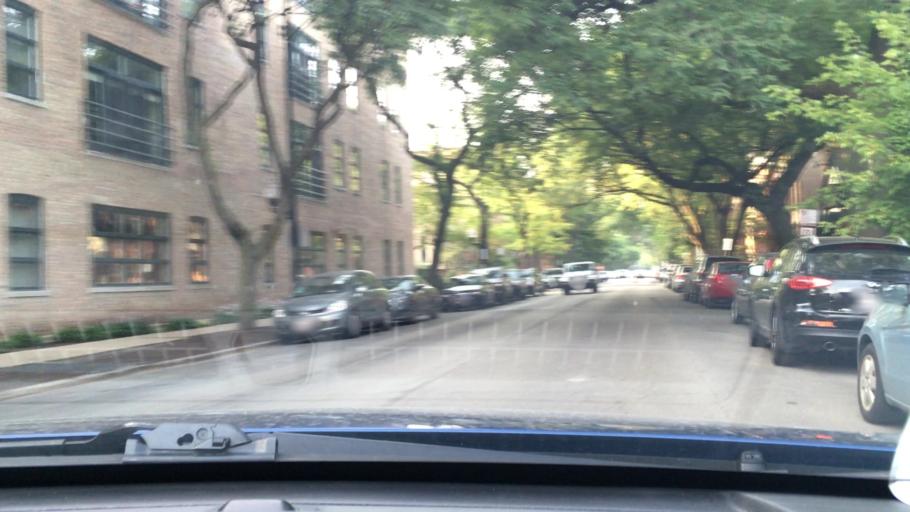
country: US
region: Illinois
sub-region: Cook County
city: Chicago
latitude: 41.9200
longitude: -87.6583
